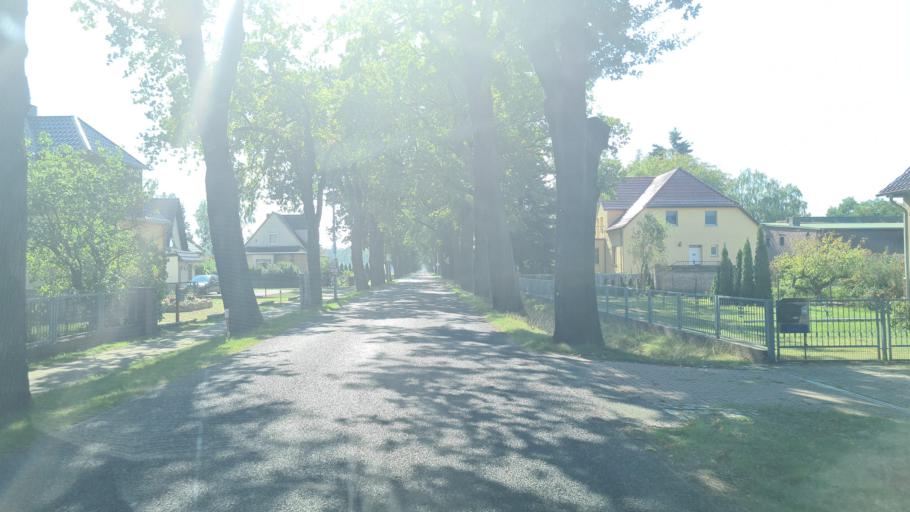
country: DE
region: Brandenburg
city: Paulinenaue
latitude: 52.6686
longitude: 12.7154
